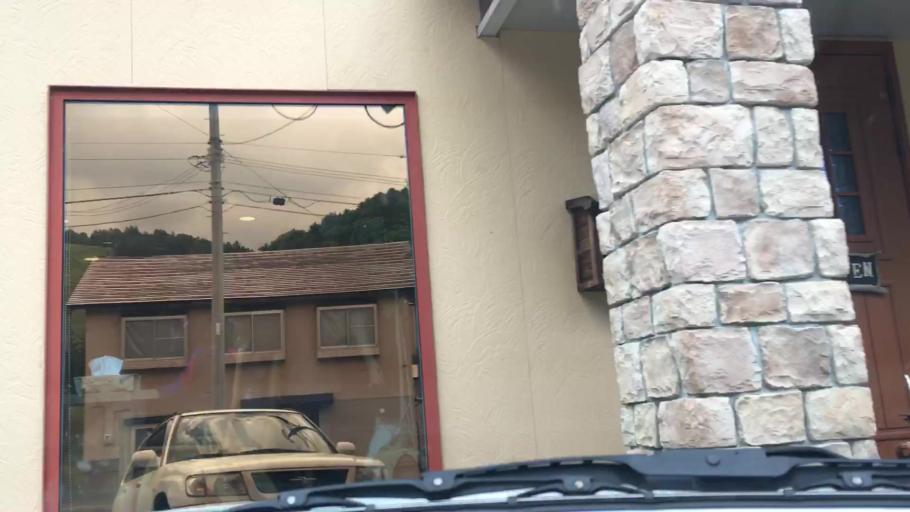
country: JP
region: Hokkaido
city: Otofuke
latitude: 43.3650
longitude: 143.1877
